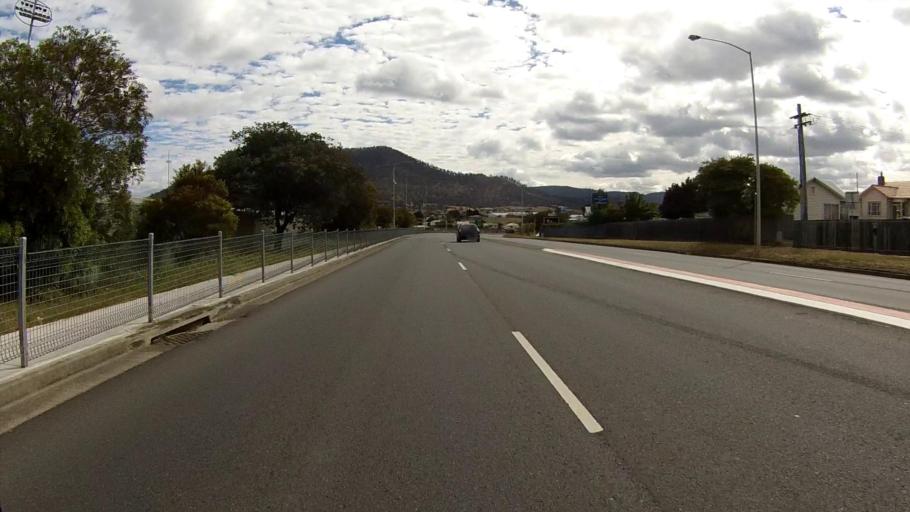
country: AU
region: Tasmania
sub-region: Glenorchy
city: Goodwood
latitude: -42.8257
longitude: 147.2896
